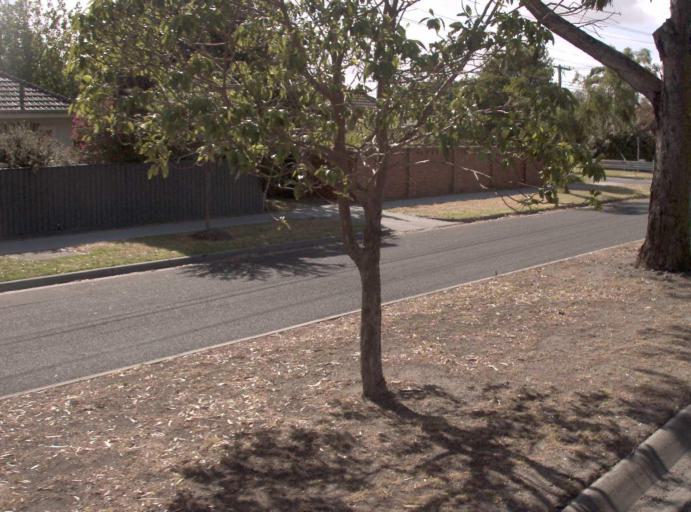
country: AU
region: Victoria
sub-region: Kingston
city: Mentone
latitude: -37.9788
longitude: 145.0685
